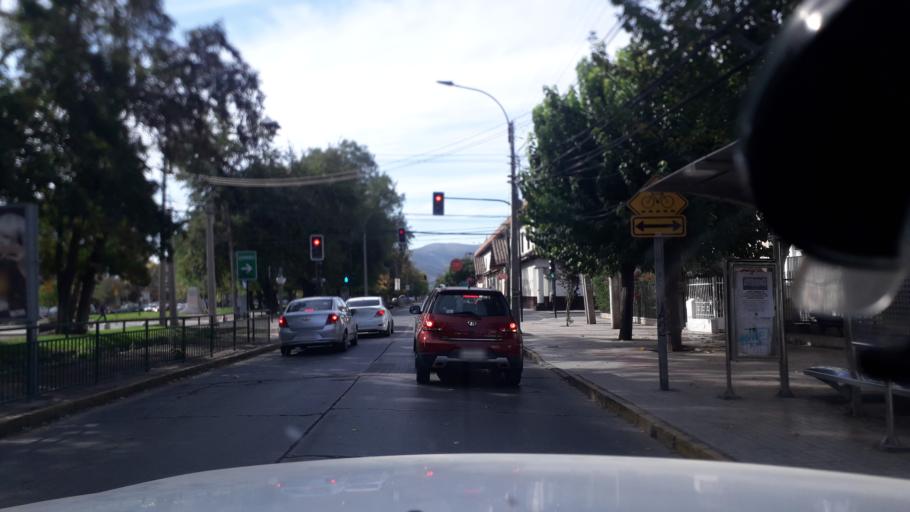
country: CL
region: Valparaiso
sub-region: Provincia de San Felipe
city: San Felipe
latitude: -32.7518
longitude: -70.7200
